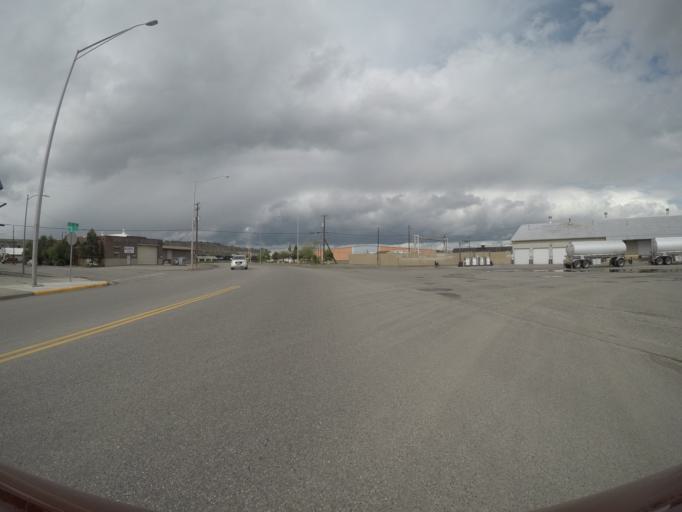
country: US
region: Montana
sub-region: Yellowstone County
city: Billings
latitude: 45.7837
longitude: -108.4950
